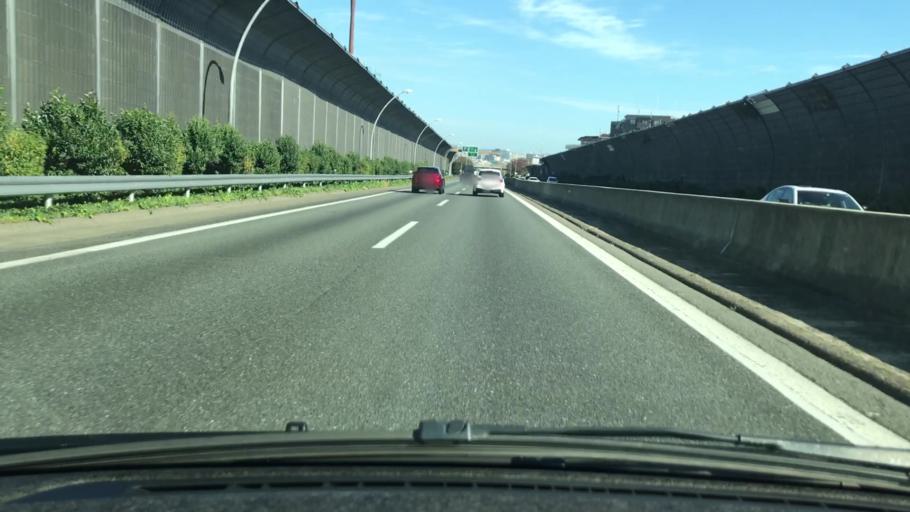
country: JP
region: Osaka
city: Suita
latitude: 34.7786
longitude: 135.5226
